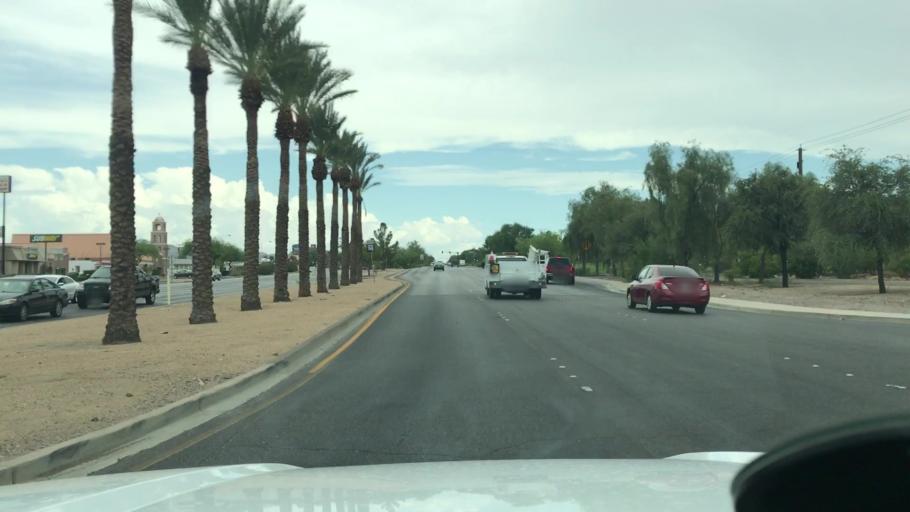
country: US
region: Nevada
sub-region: Clark County
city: Henderson
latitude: 36.0393
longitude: -114.9819
